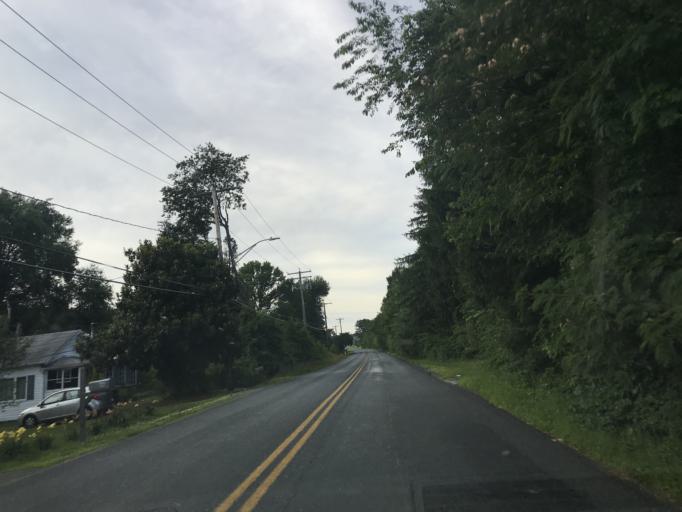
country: US
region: Maryland
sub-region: Harford County
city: Perryman
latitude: 39.4954
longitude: -76.2111
